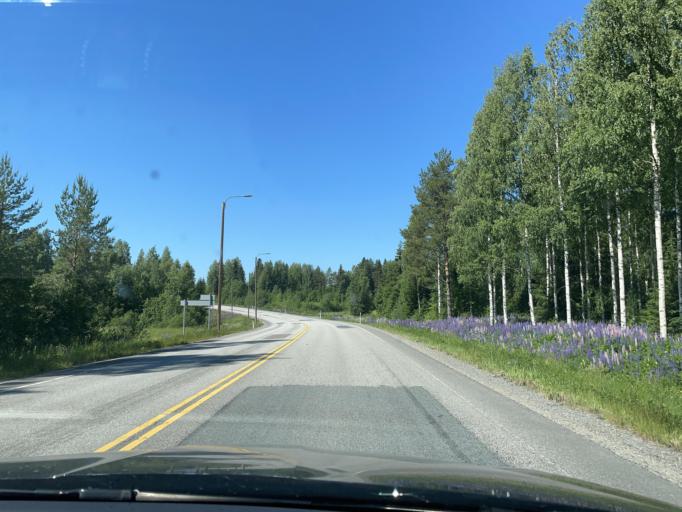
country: FI
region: Central Finland
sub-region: Saarijaervi-Viitasaari
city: Viitasaari
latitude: 63.1451
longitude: 25.8092
